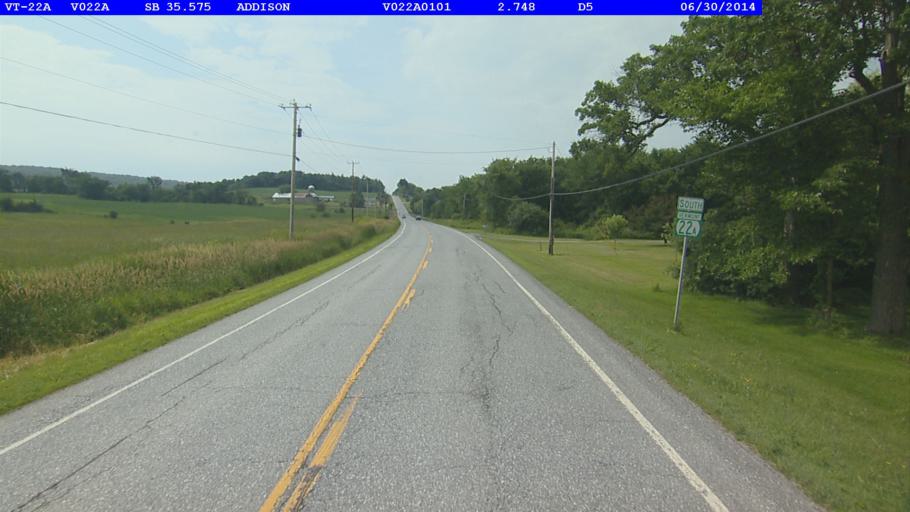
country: US
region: Vermont
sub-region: Addison County
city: Vergennes
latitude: 44.0690
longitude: -73.3043
